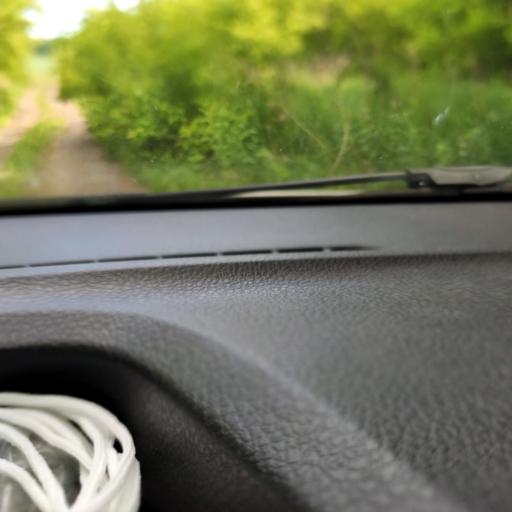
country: RU
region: Bashkortostan
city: Mikhaylovka
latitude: 54.8307
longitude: 55.7360
